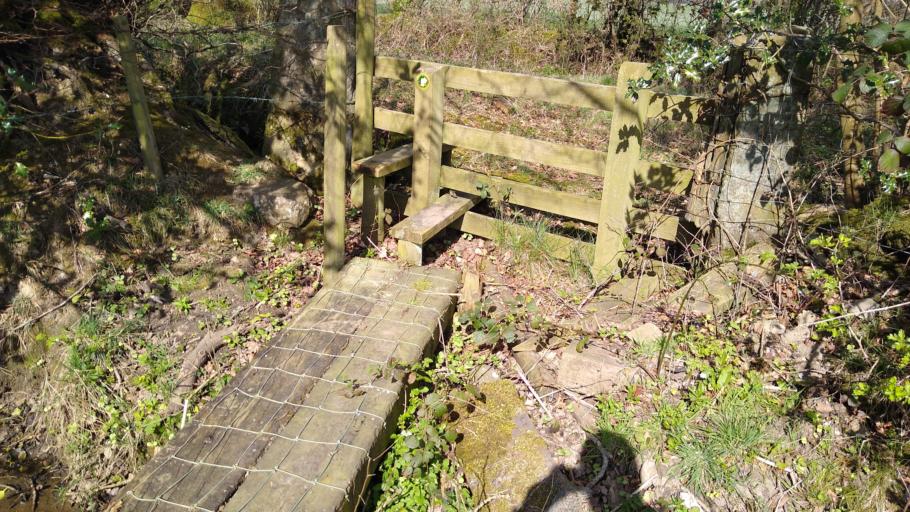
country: GB
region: England
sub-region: Cumbria
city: Dearham
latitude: 54.7155
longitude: -3.4016
